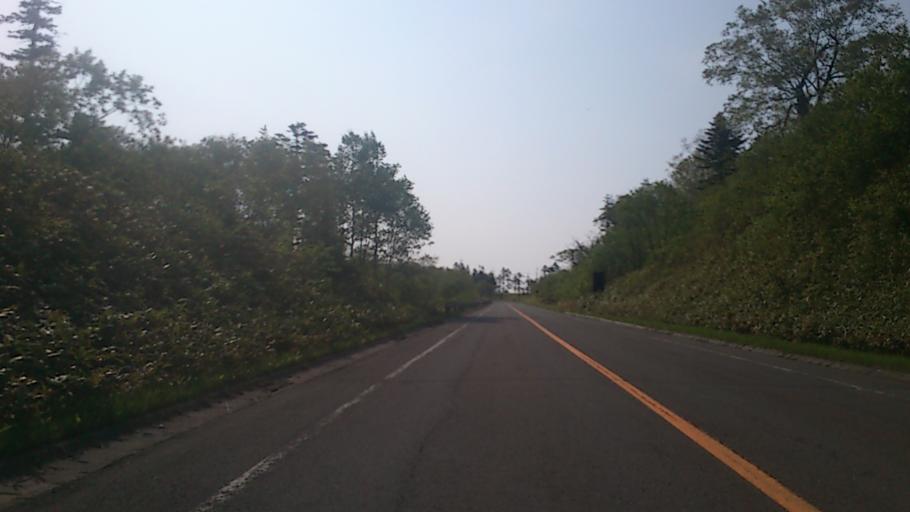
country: JP
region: Hokkaido
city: Bihoro
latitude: 43.4476
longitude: 144.2065
